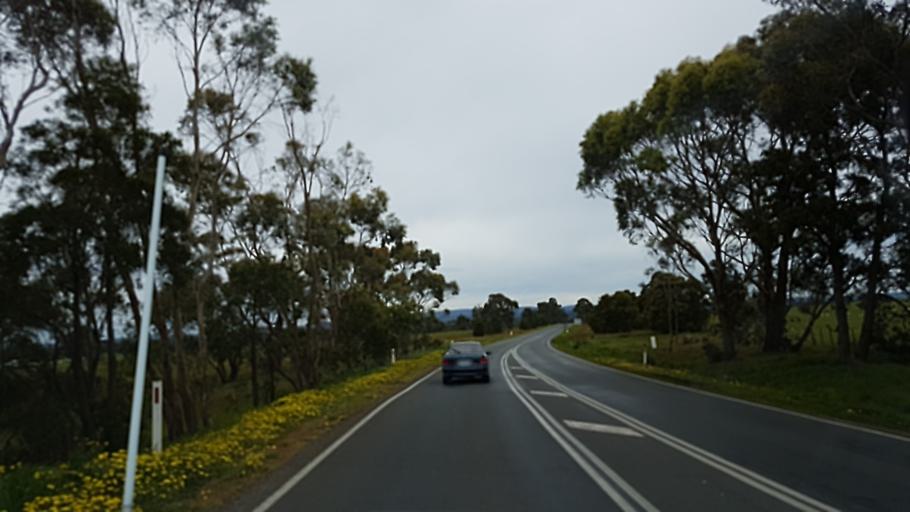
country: AU
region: Victoria
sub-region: Moorabool
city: Bacchus Marsh
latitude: -37.6233
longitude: 144.2106
